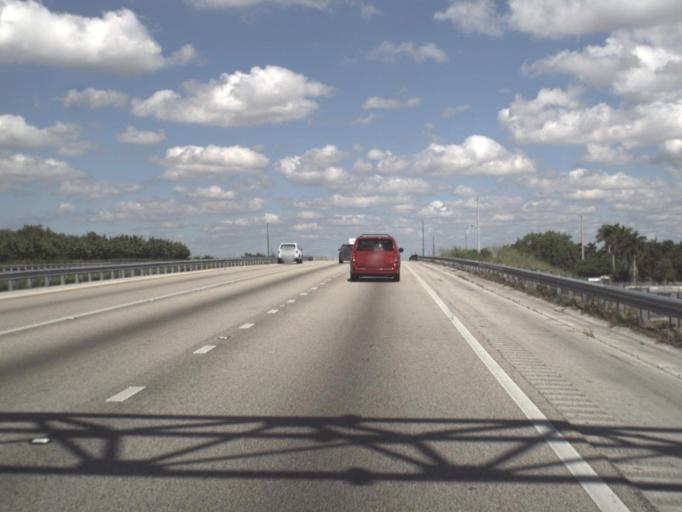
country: US
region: Florida
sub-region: Miami-Dade County
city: Westwood Lake
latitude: 25.7133
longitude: -80.3834
